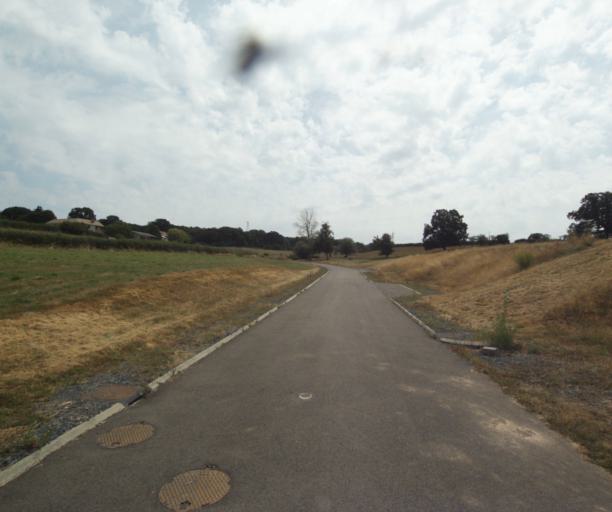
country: FR
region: Bourgogne
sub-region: Departement de Saone-et-Loire
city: Gueugnon
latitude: 46.5903
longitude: 4.0704
